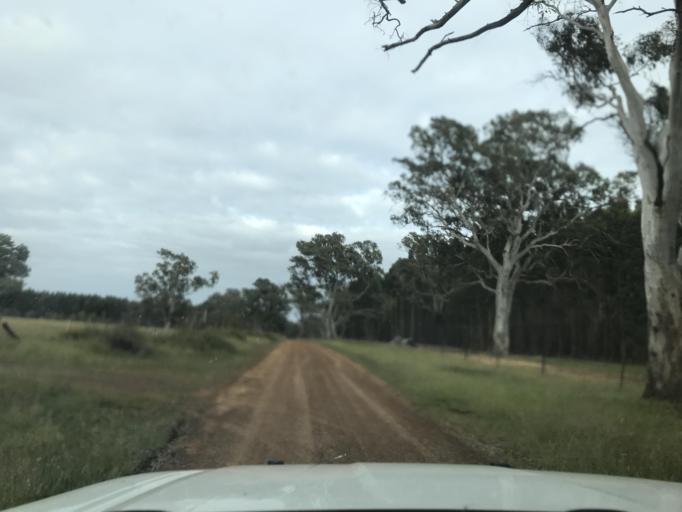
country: AU
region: South Australia
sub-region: Wattle Range
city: Penola
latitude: -37.2795
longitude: 141.3924
